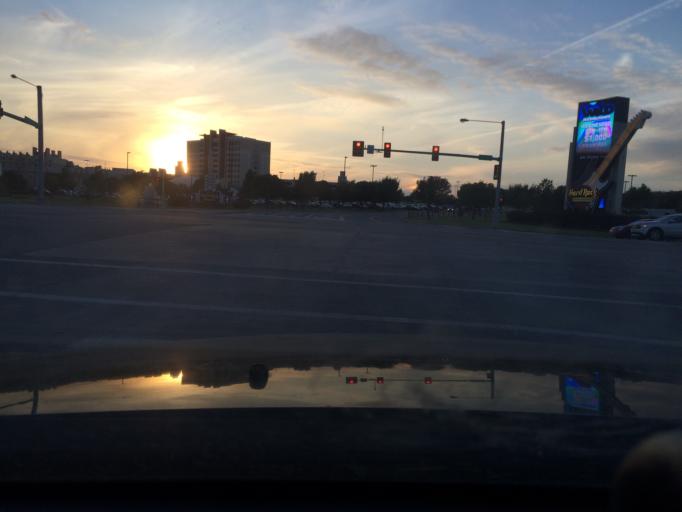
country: US
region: Oklahoma
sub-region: Rogers County
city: Catoosa
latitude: 36.1669
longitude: -95.7611
